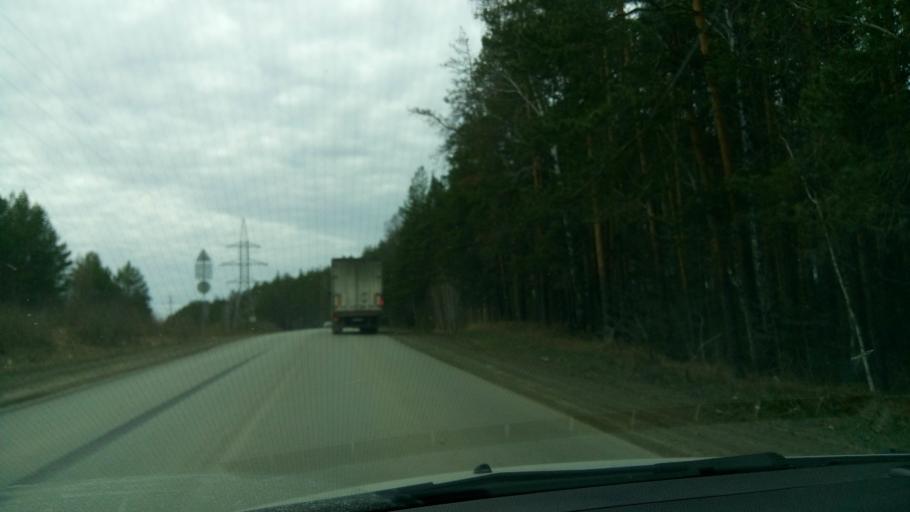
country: RU
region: Sverdlovsk
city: Verkhnyaya Pyshma
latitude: 56.9547
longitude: 60.6496
